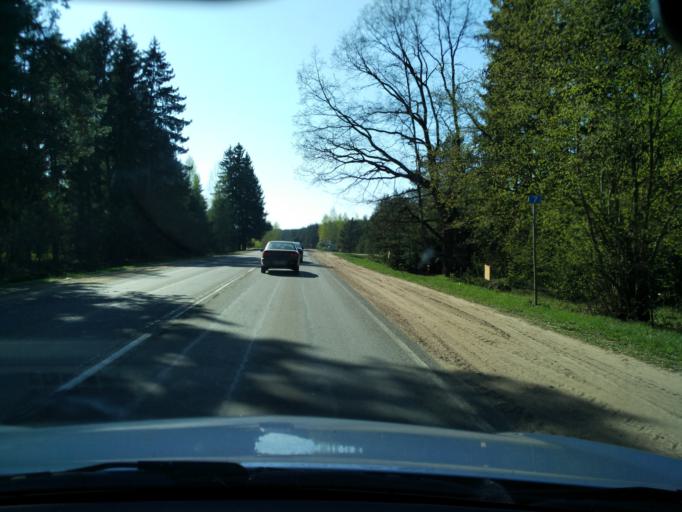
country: BY
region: Minsk
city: Lyeskawka
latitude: 53.9606
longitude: 27.7122
